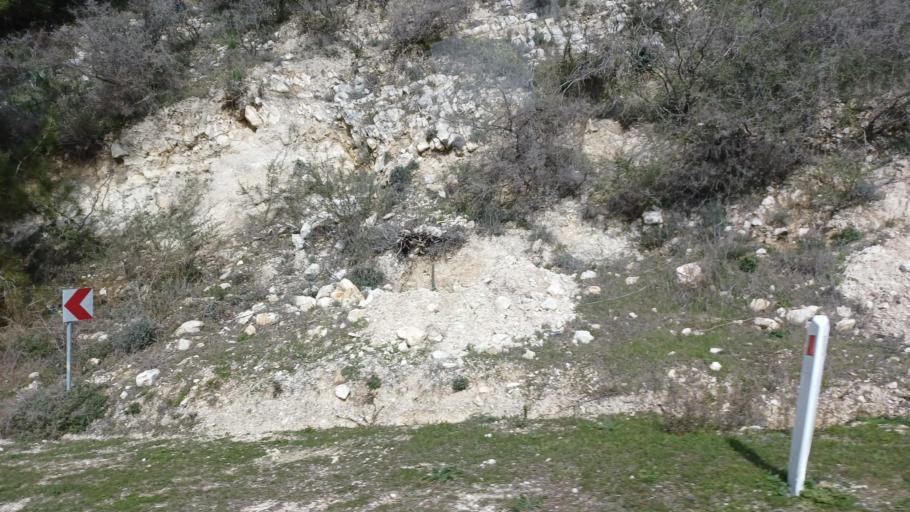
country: CY
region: Limassol
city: Pissouri
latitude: 34.7537
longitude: 32.6843
